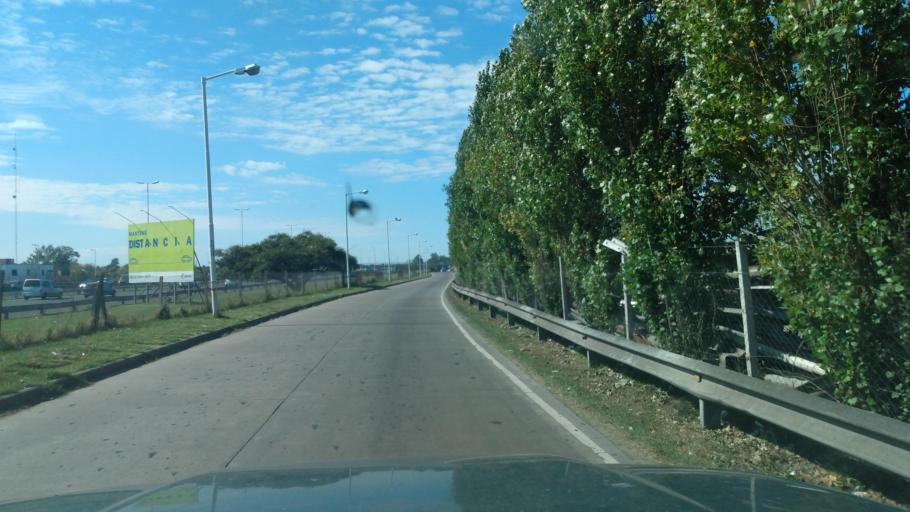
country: AR
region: Buenos Aires
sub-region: Partido de Merlo
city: Merlo
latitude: -34.6285
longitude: -58.7284
